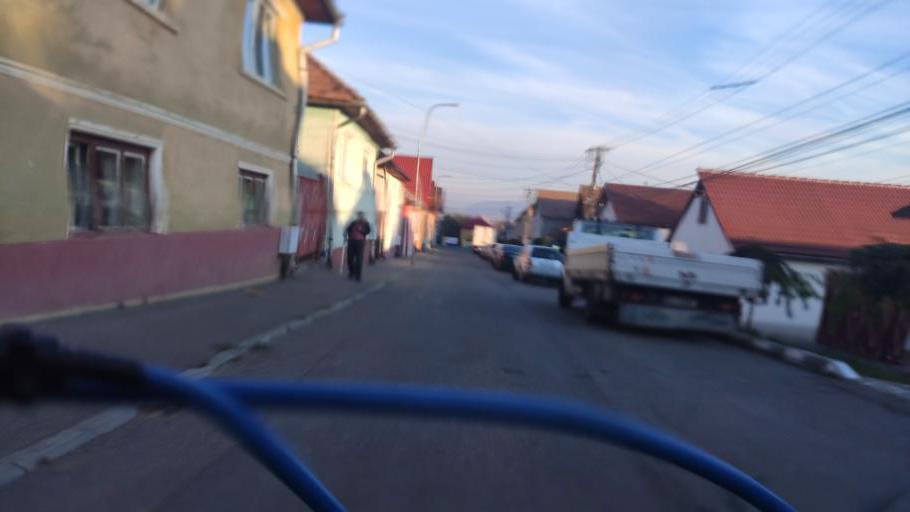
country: RO
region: Brasov
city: Codlea
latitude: 45.7064
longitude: 25.4483
